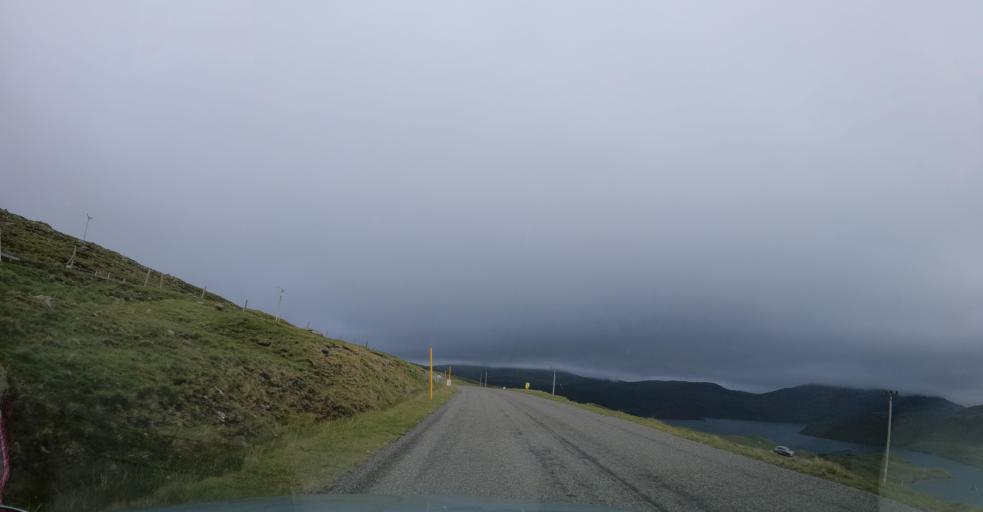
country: GB
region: Scotland
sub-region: Eilean Siar
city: Harris
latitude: 57.9581
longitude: -6.7492
